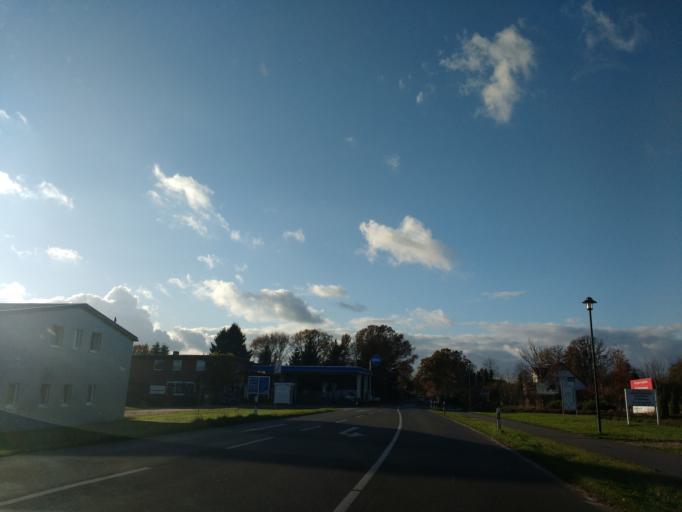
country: DE
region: Lower Saxony
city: Egestorf
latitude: 53.1941
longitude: 10.0735
